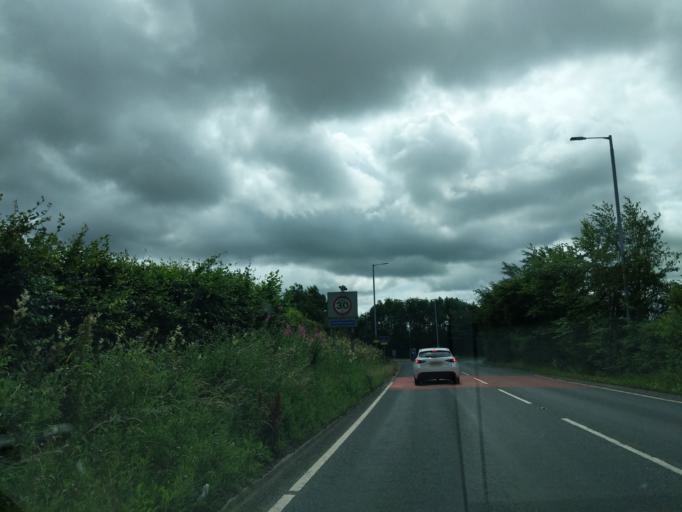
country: GB
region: Scotland
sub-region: South Lanarkshire
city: Stonehouse
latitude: 55.6973
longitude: -3.9906
